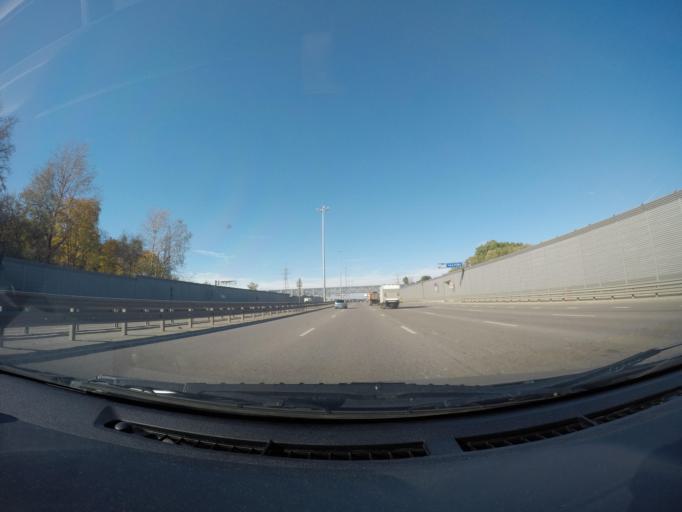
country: RU
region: Moskovskaya
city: Tomilino
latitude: 55.6319
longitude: 37.9368
